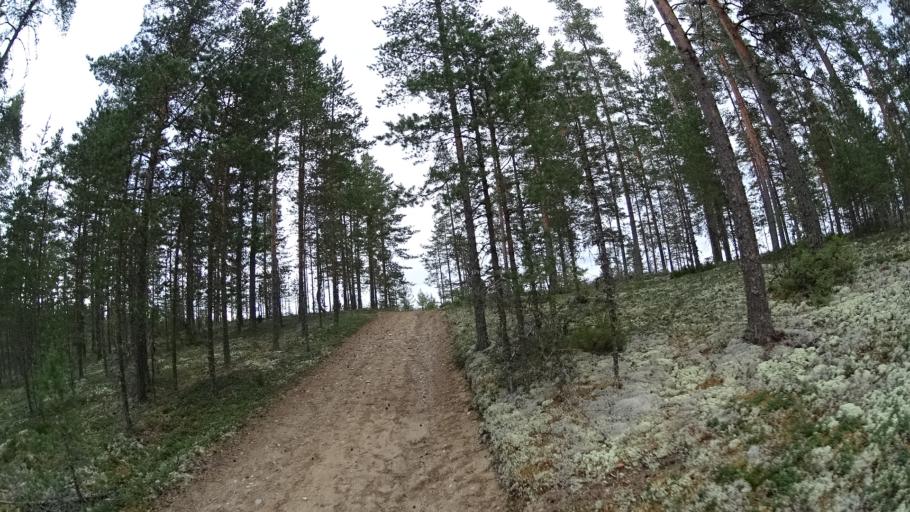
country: FI
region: Satakunta
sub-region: Pohjois-Satakunta
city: Jaemijaervi
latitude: 61.7694
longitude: 22.7911
